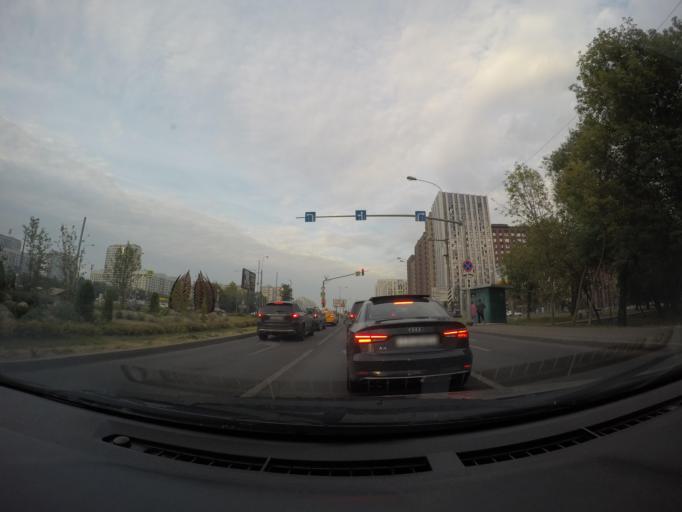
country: RU
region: Moscow
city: Orekhovo-Borisovo
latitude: 55.6008
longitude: 37.7215
